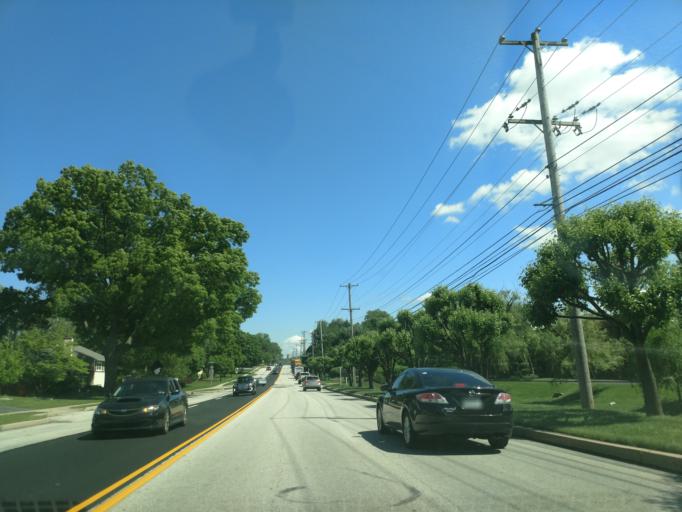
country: US
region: Pennsylvania
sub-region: Montgomery County
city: King of Prussia
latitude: 40.0965
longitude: -75.3918
